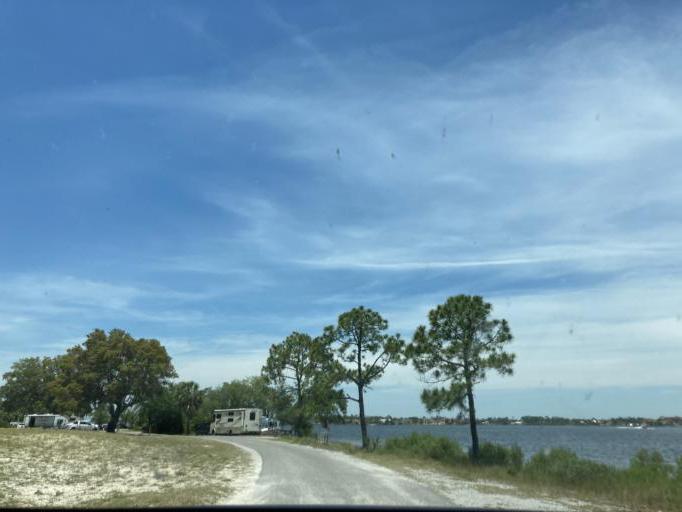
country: US
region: Florida
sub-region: Bay County
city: Lower Grand Lagoon
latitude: 30.1354
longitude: -85.7339
